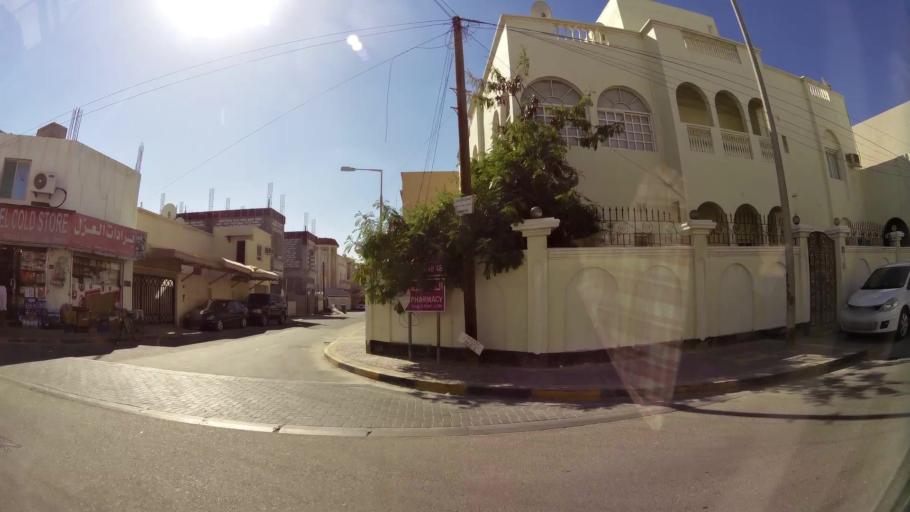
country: BH
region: Muharraq
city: Al Hadd
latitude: 26.2362
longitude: 50.6554
